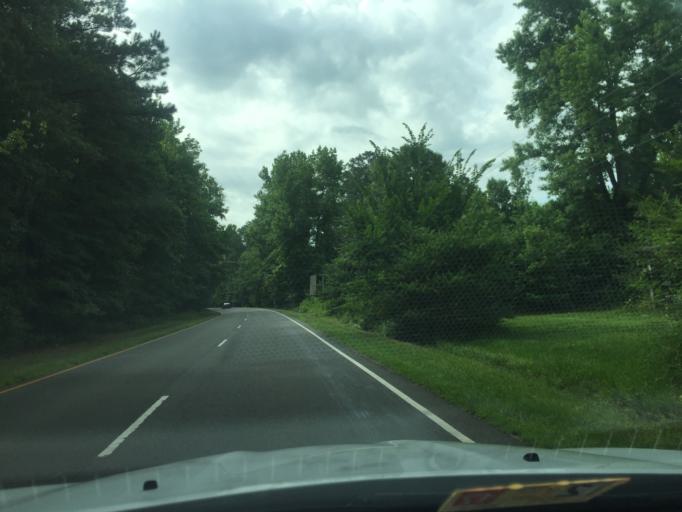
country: US
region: Virginia
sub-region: Charles City County
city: Charles City
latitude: 37.4515
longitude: -77.0779
